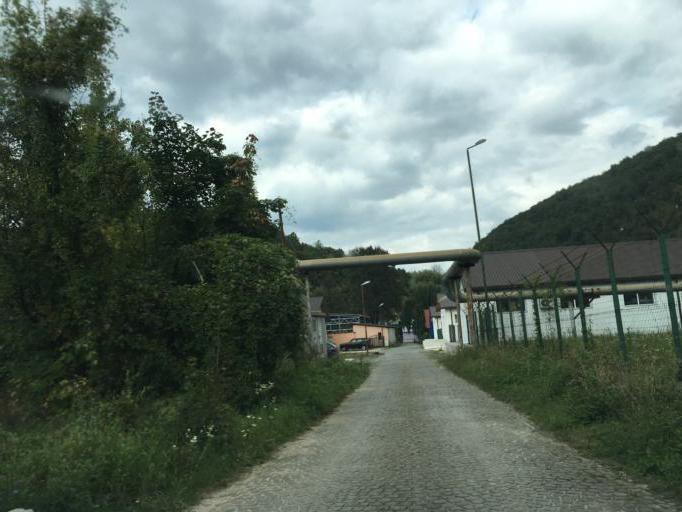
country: BA
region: Federation of Bosnia and Herzegovina
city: Novi Travnik
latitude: 44.1629
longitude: 17.6447
